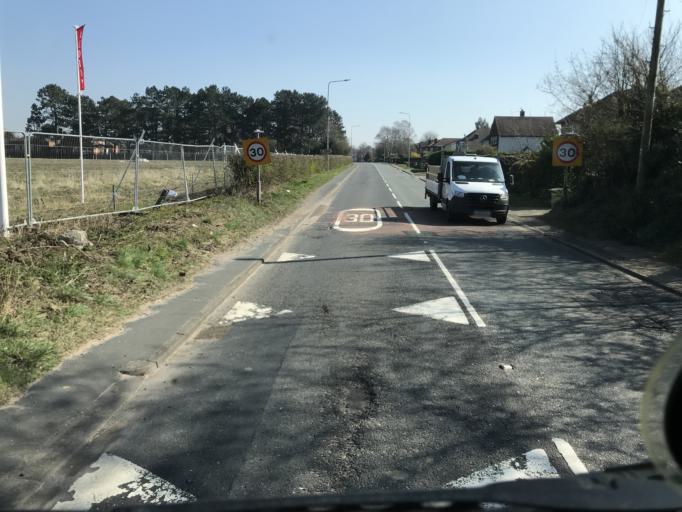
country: GB
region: England
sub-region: Cheshire East
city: Knutsford
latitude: 53.3029
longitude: -2.3896
